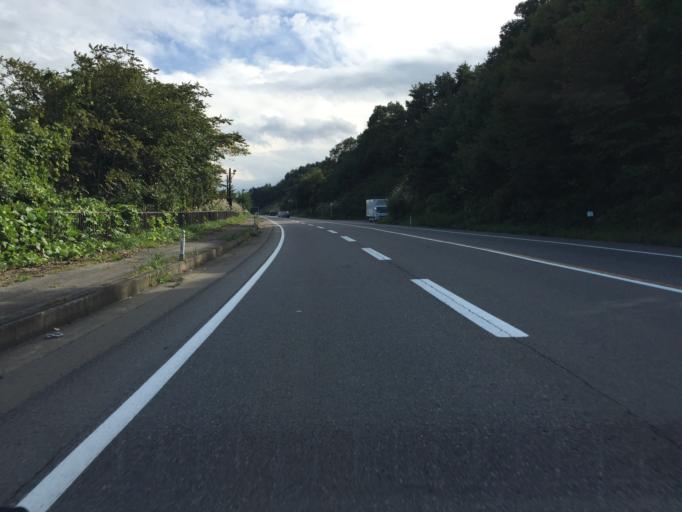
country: JP
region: Fukushima
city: Inawashiro
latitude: 37.5270
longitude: 139.9806
